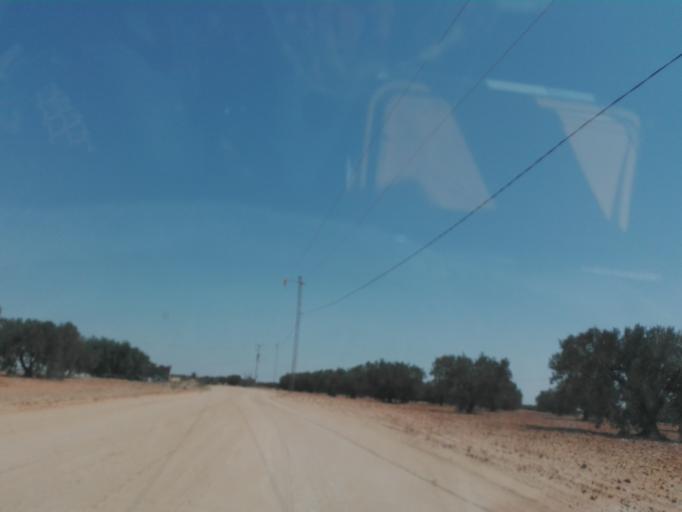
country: TN
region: Safaqis
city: Bi'r `Ali Bin Khalifah
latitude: 34.6684
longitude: 10.2365
